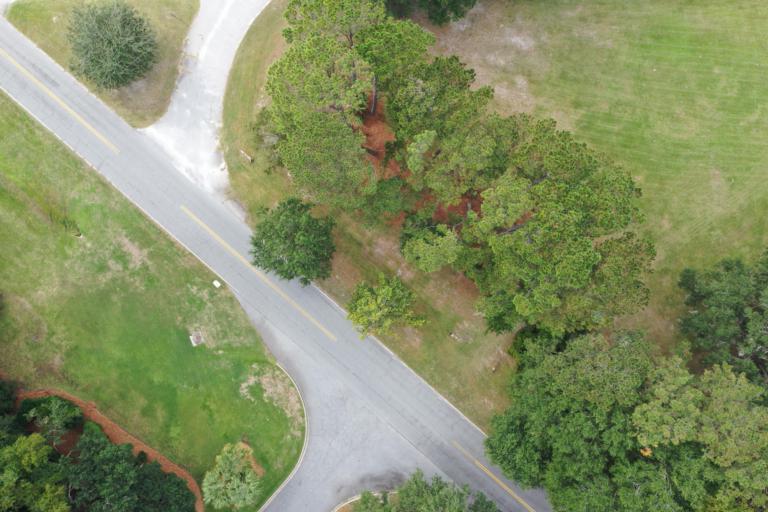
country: US
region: Georgia
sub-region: Chatham County
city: Isle of Hope
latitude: 31.9860
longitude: -81.0230
